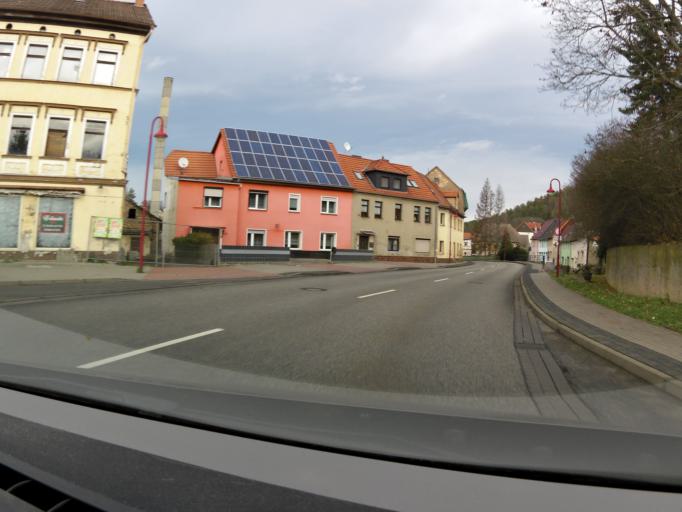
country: DE
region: Saxony-Anhalt
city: Mansfeld
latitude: 51.5956
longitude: 11.4556
